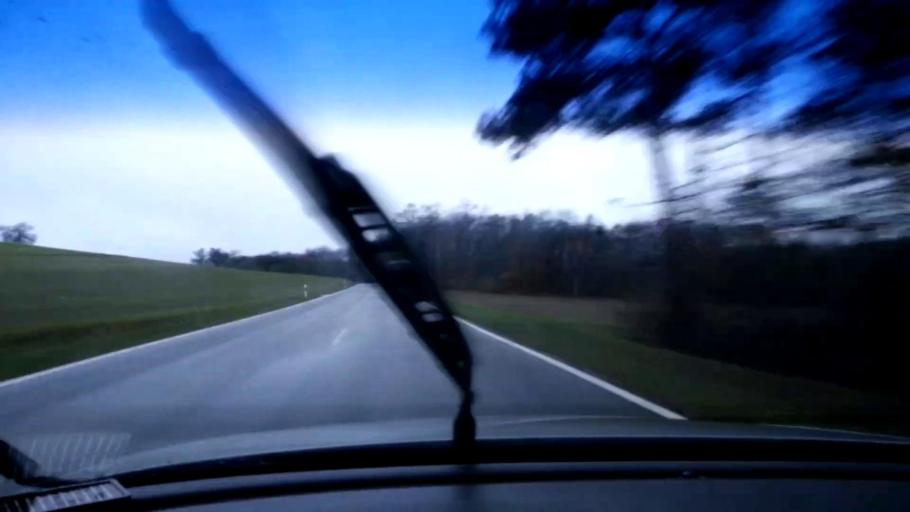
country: DE
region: Bavaria
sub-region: Upper Franconia
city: Zapfendorf
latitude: 49.9938
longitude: 10.9616
